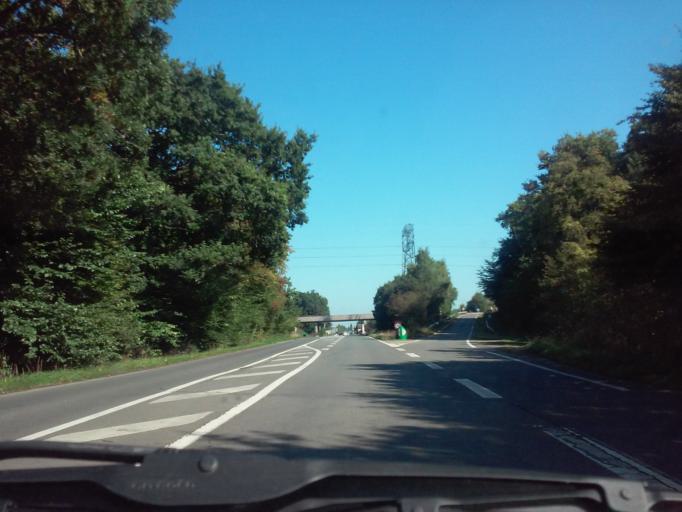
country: FR
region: Brittany
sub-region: Departement d'Ille-et-Vilaine
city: Betton
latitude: 48.1581
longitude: -1.6497
